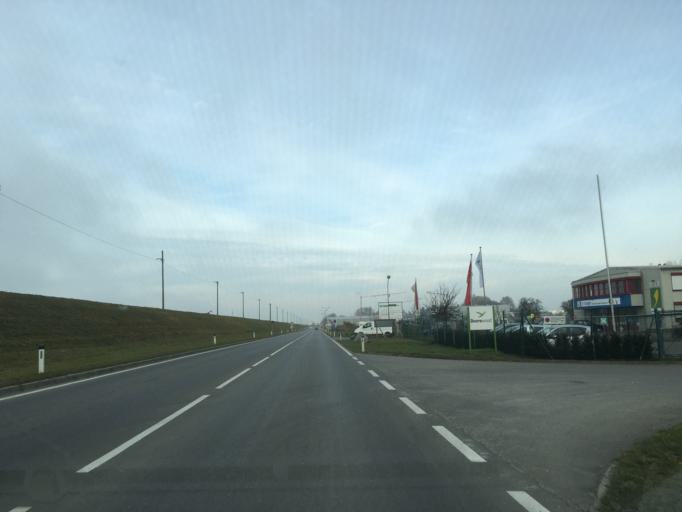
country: AT
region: Vorarlberg
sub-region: Politischer Bezirk Bregenz
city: Fussach
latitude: 47.4712
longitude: 9.6711
